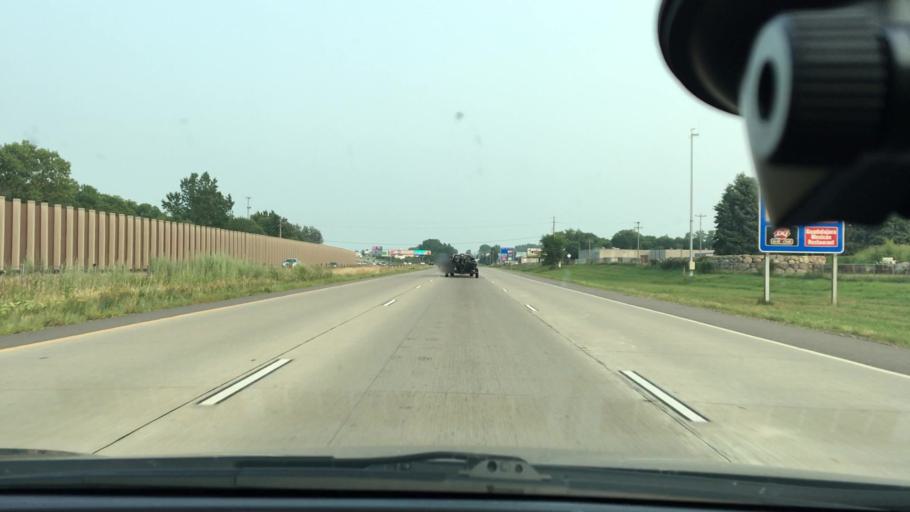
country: US
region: Minnesota
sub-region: Hennepin County
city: Rogers
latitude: 45.2044
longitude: -93.5738
